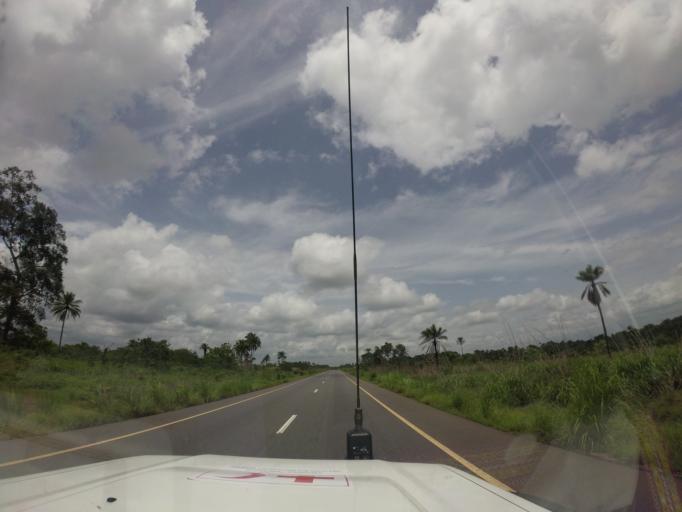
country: SL
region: Northern Province
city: Port Loko
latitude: 8.8471
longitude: -12.7682
